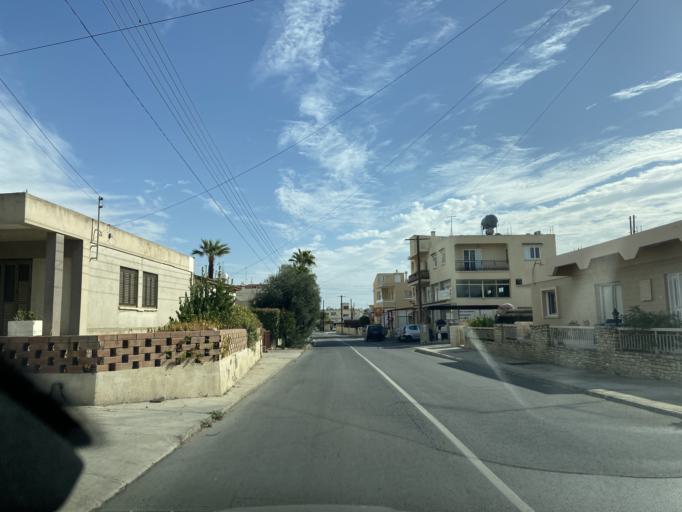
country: CY
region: Lefkosia
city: Dali
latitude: 35.0168
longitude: 33.3953
